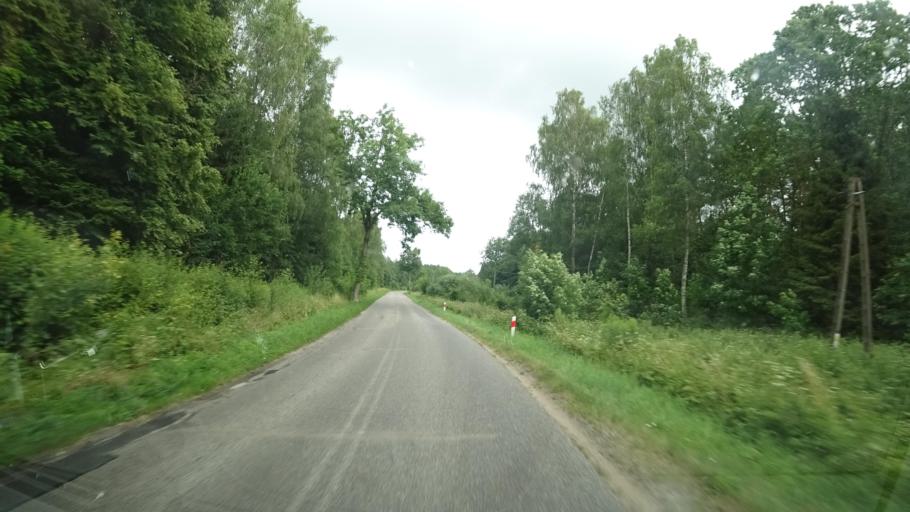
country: PL
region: Warmian-Masurian Voivodeship
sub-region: Powiat goldapski
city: Goldap
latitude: 54.3089
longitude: 22.3860
